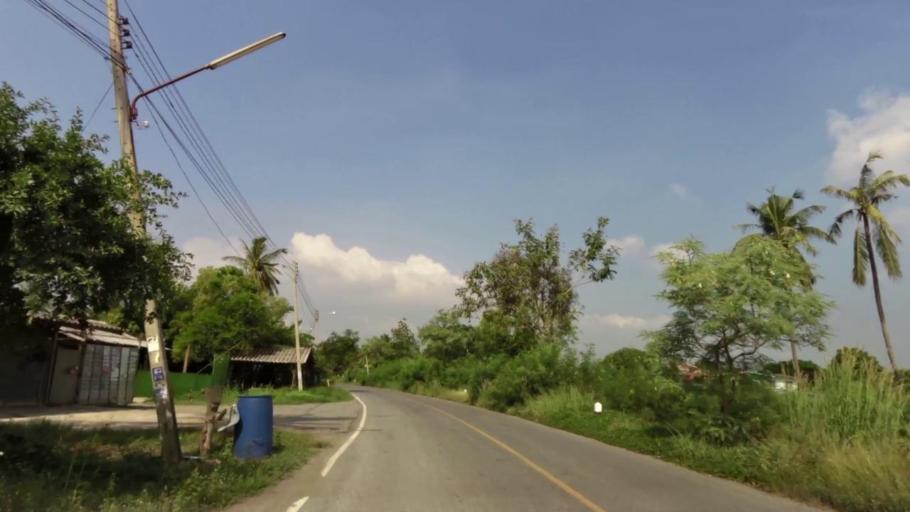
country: TH
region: Ang Thong
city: Ang Thong
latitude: 14.5994
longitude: 100.4015
